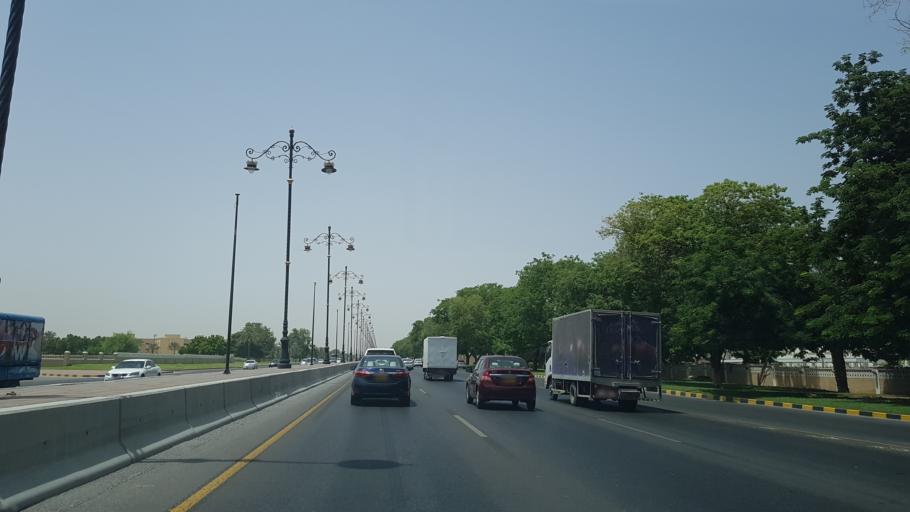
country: OM
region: Muhafazat Masqat
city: Bawshar
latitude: 23.5853
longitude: 58.2855
